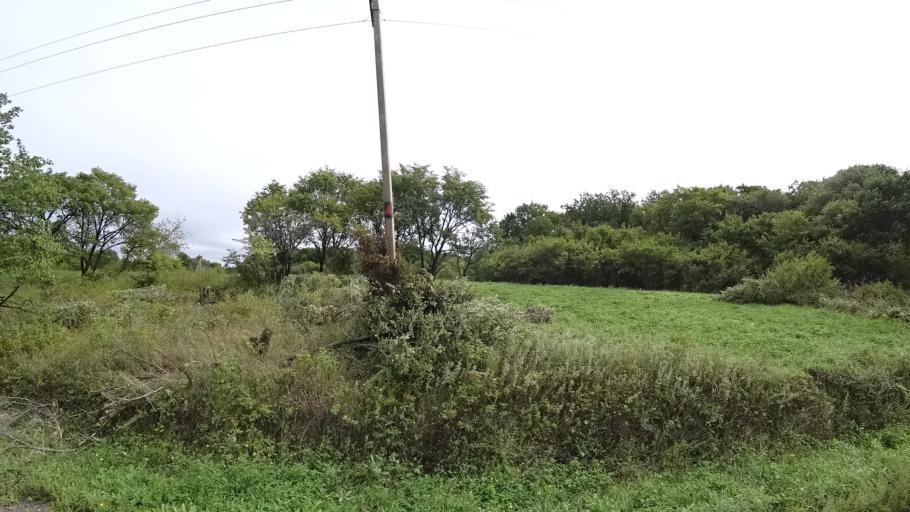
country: RU
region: Primorskiy
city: Lyalichi
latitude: 44.0748
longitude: 132.4689
